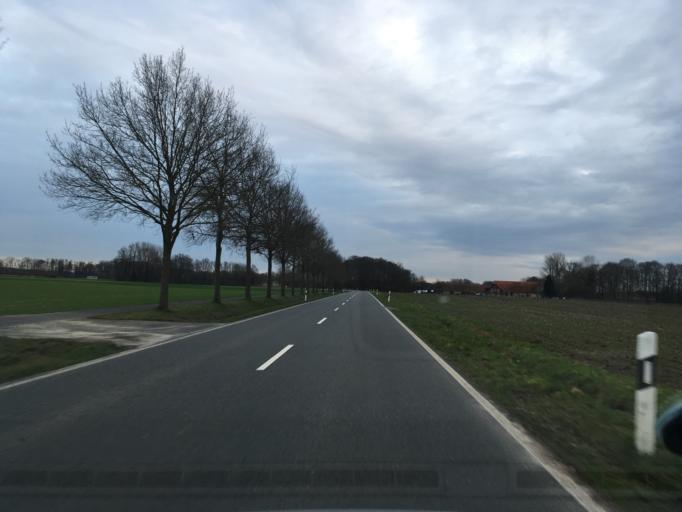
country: DE
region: North Rhine-Westphalia
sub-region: Regierungsbezirk Munster
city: Schoppingen
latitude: 52.0724
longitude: 7.2376
